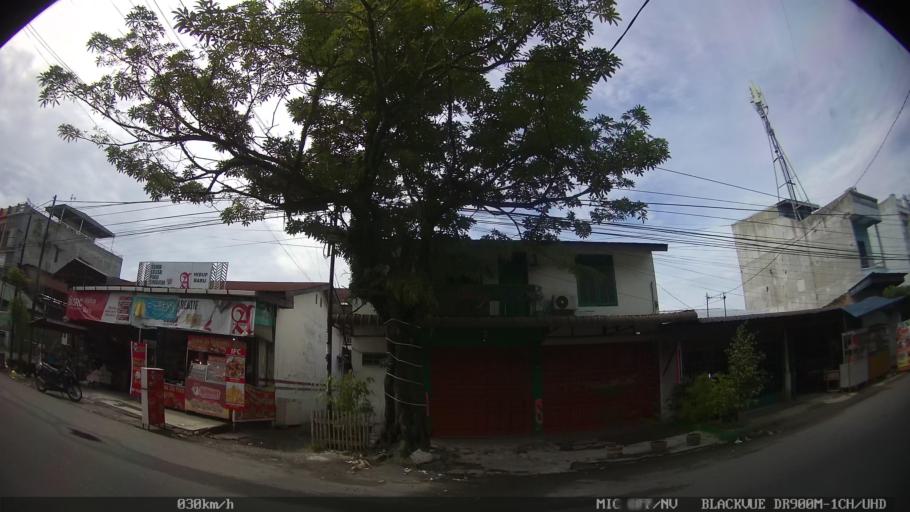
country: ID
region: North Sumatra
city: Medan
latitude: 3.6228
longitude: 98.6830
